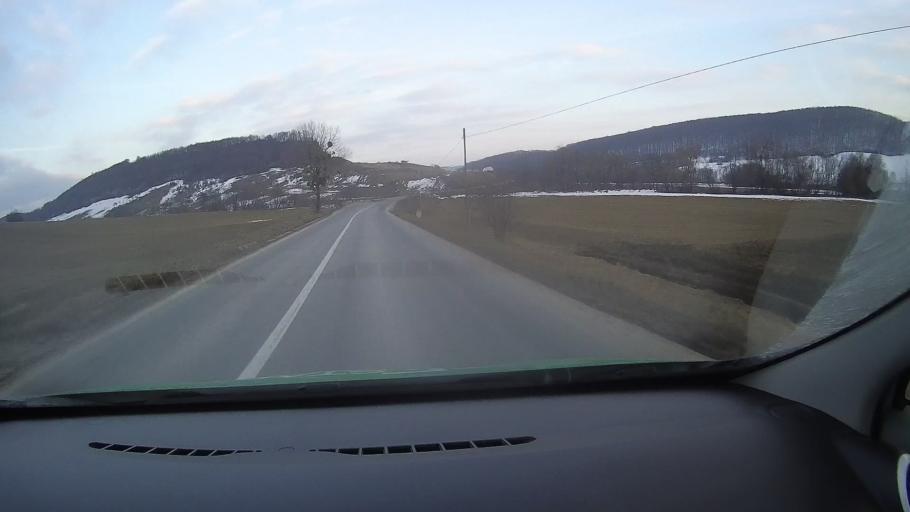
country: RO
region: Harghita
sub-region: Comuna Lupeni
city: Lupeni
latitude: 46.3608
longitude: 25.1857
